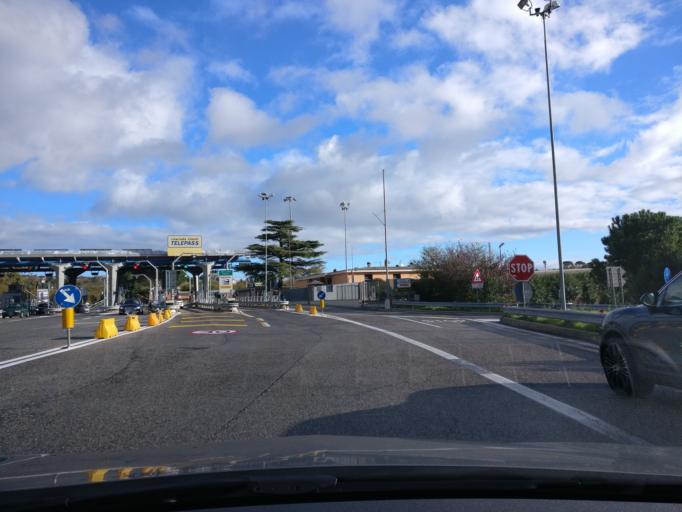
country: IT
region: Campania
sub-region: Provincia di Avellino
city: Torelli-Torrette
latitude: 40.9084
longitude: 14.7489
